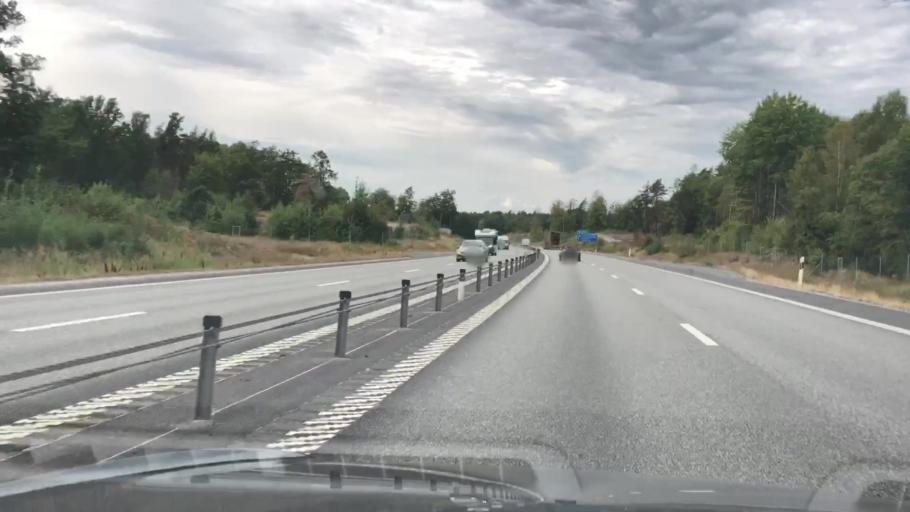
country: SE
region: Blekinge
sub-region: Karlshamns Kommun
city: Morrum
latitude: 56.1753
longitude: 14.6975
